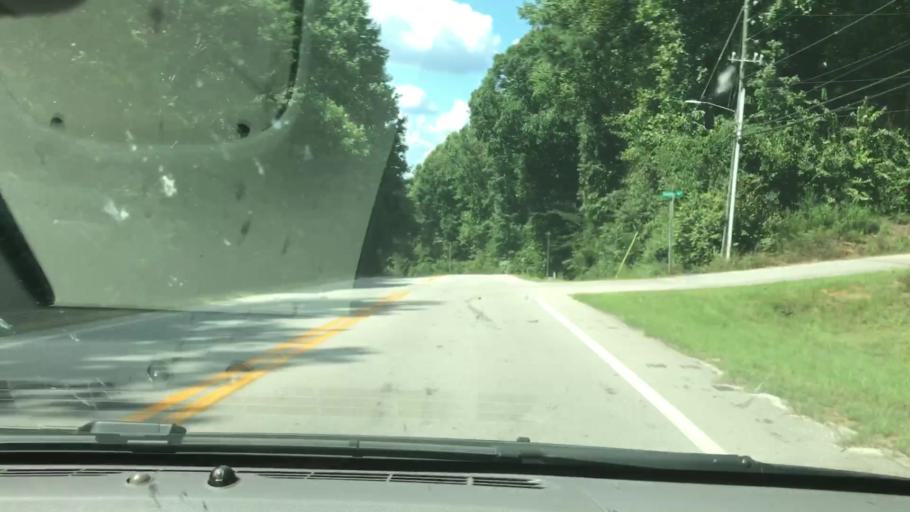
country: US
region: Georgia
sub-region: Troup County
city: La Grange
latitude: 33.0711
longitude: -85.0419
